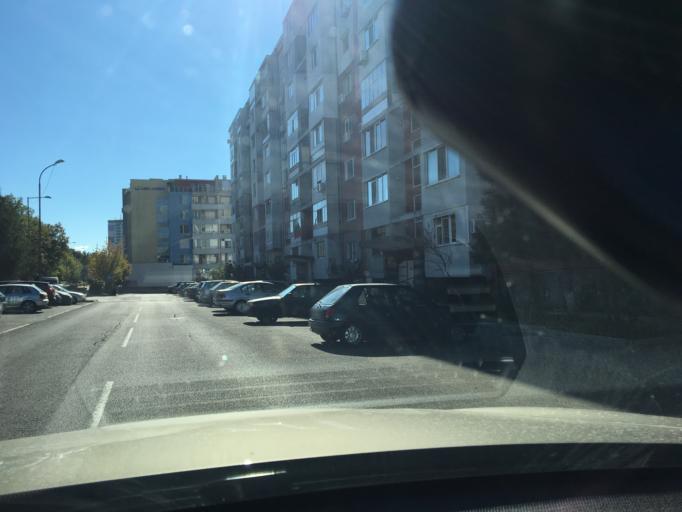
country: BG
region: Burgas
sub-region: Obshtina Burgas
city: Burgas
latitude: 42.5190
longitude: 27.4515
